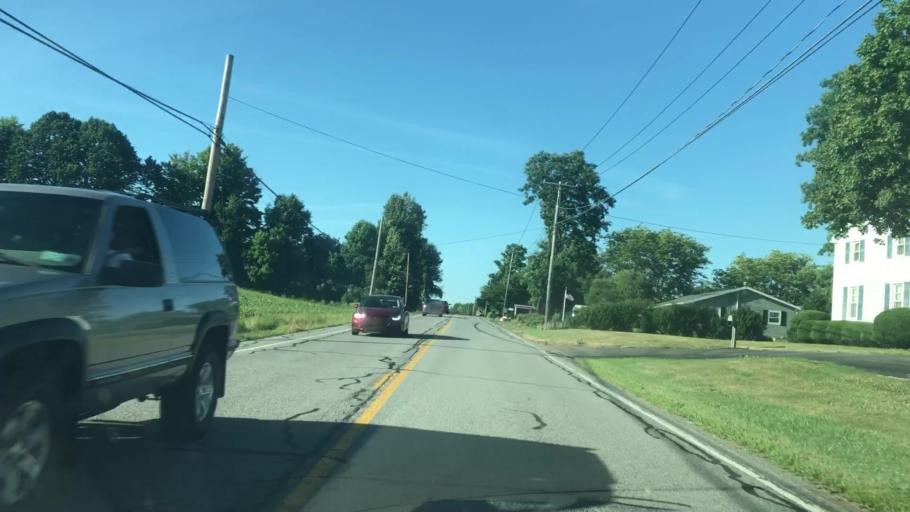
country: US
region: New York
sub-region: Wayne County
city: Ontario
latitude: 43.1734
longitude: -77.2873
